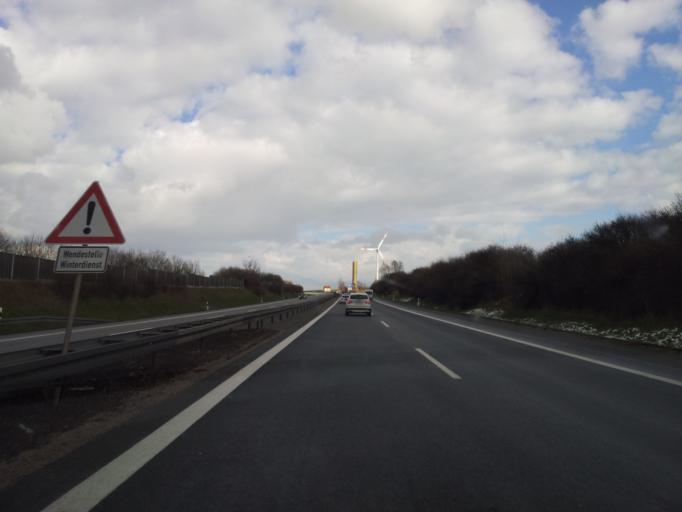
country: DE
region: Saxony
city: Reinsdorf
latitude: 50.6759
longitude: 12.5541
